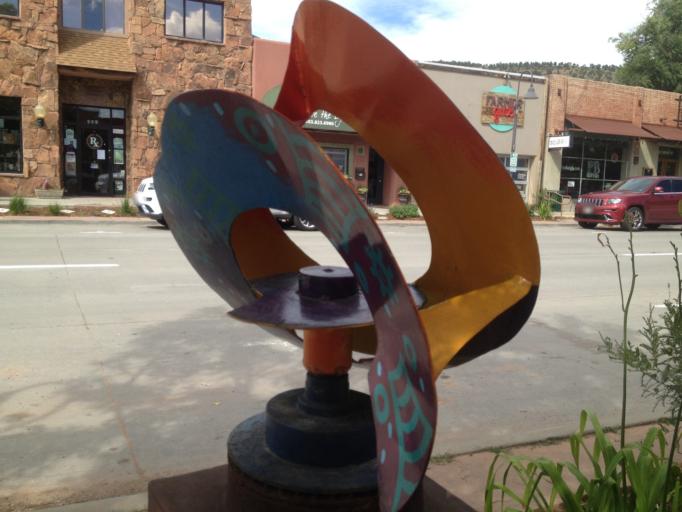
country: US
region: Colorado
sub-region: Boulder County
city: Lyons
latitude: 40.2246
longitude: -105.2710
